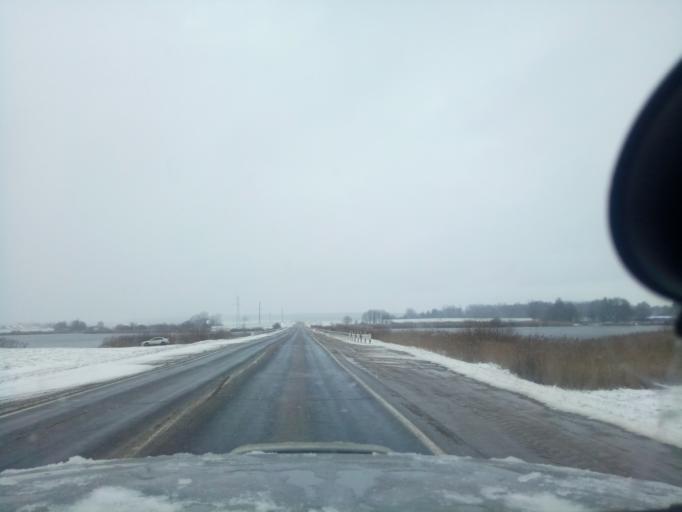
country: BY
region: Minsk
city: Nyasvizh
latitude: 53.2078
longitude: 26.6640
